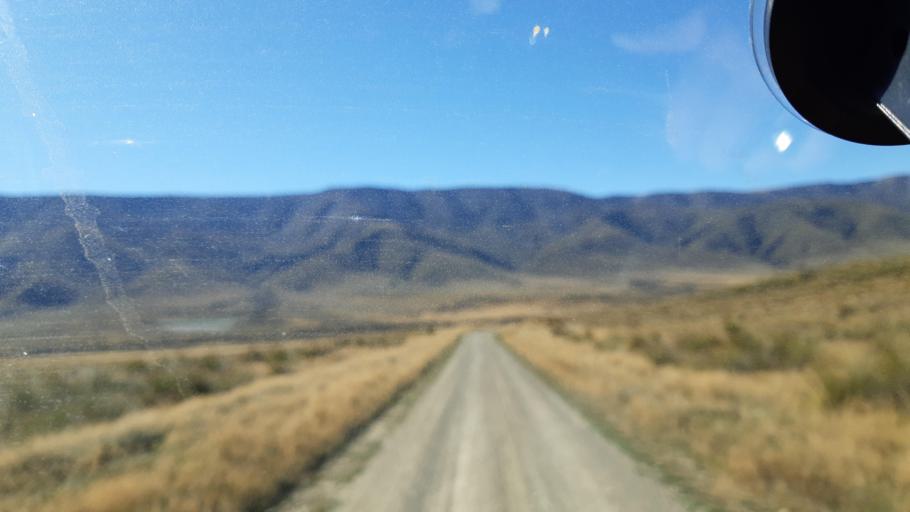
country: NZ
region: Otago
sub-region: Queenstown-Lakes District
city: Wanaka
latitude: -44.7771
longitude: 169.9002
